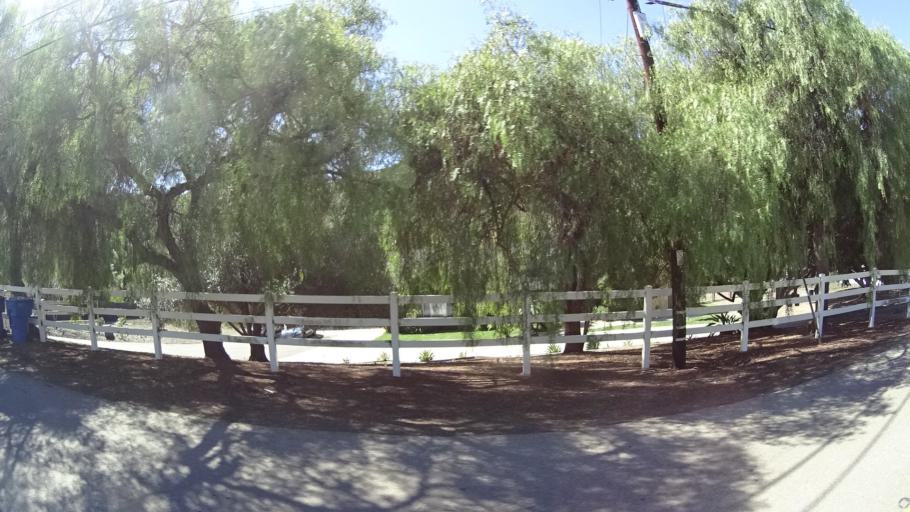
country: US
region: California
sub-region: San Diego County
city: Bonita
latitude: 32.6602
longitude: -117.0205
